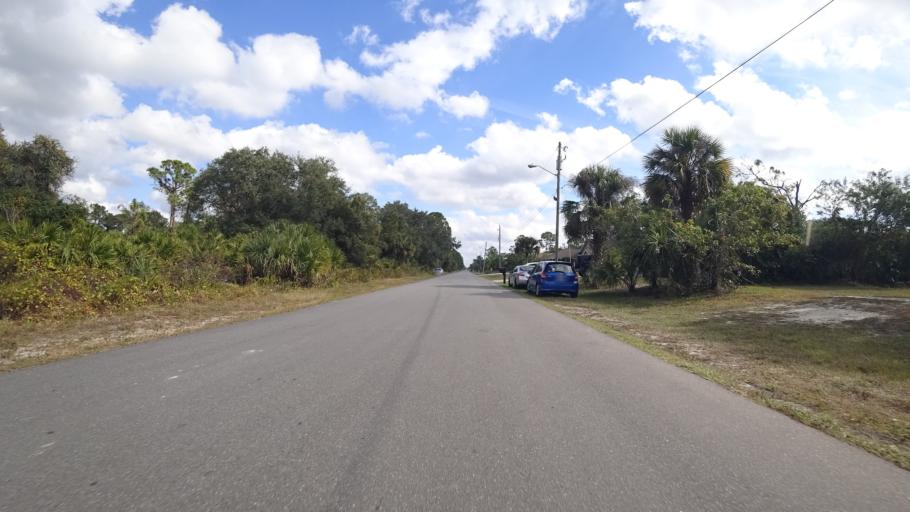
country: US
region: Florida
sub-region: Charlotte County
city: Port Charlotte
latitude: 27.0339
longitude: -82.1375
